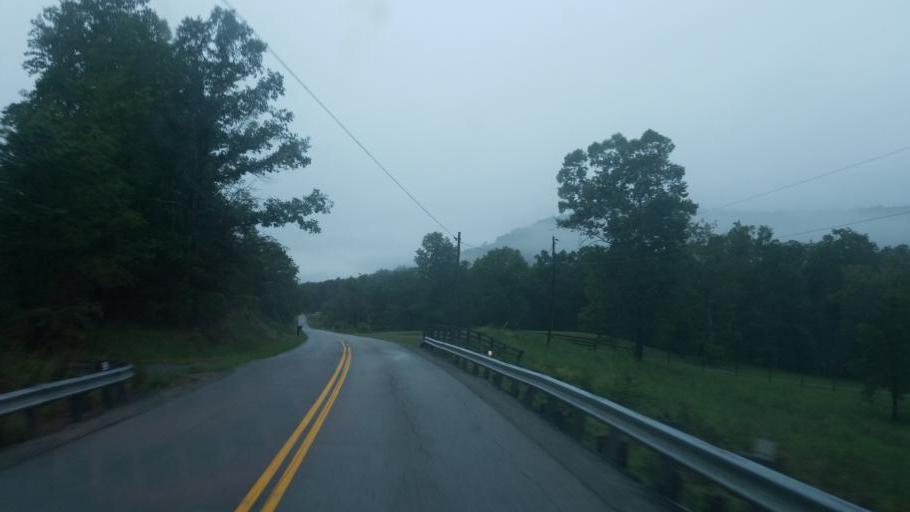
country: US
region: Kentucky
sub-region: Fleming County
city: Flemingsburg
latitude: 38.4062
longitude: -83.5870
